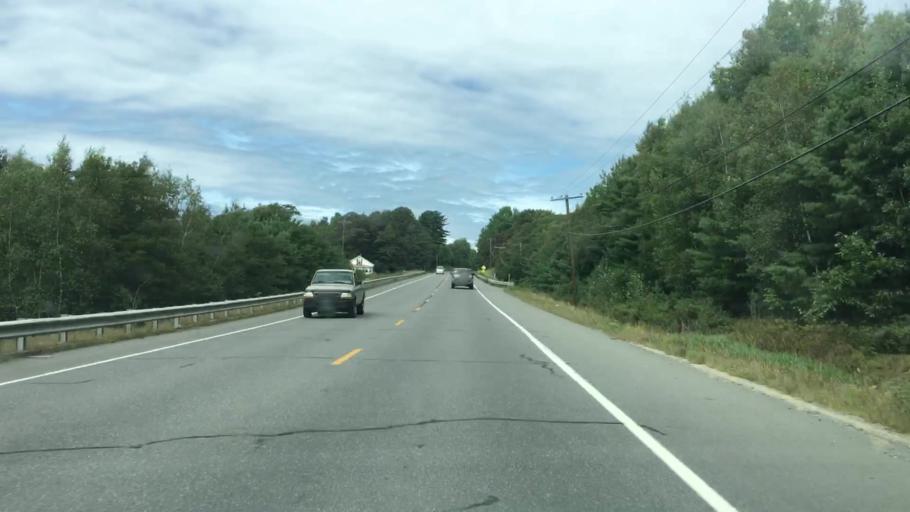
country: US
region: Maine
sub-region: Piscataquis County
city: Milo
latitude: 45.2777
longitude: -69.0053
